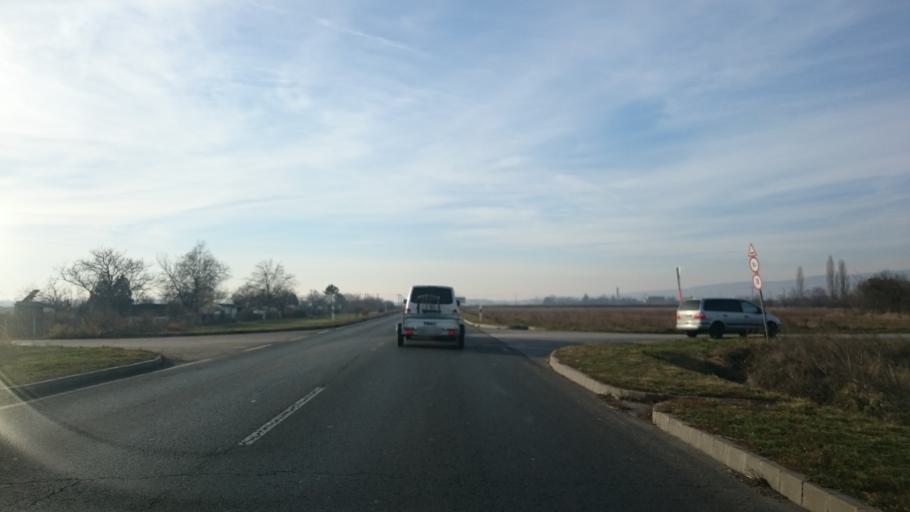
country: HU
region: Baranya
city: Pellerd
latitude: 46.0550
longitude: 18.1881
